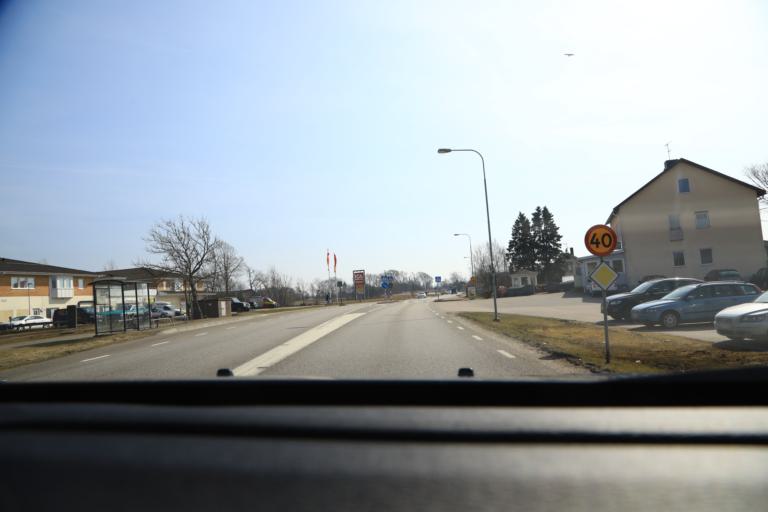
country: SE
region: Halland
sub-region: Kungsbacka Kommun
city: Frillesas
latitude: 57.2501
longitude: 12.1822
